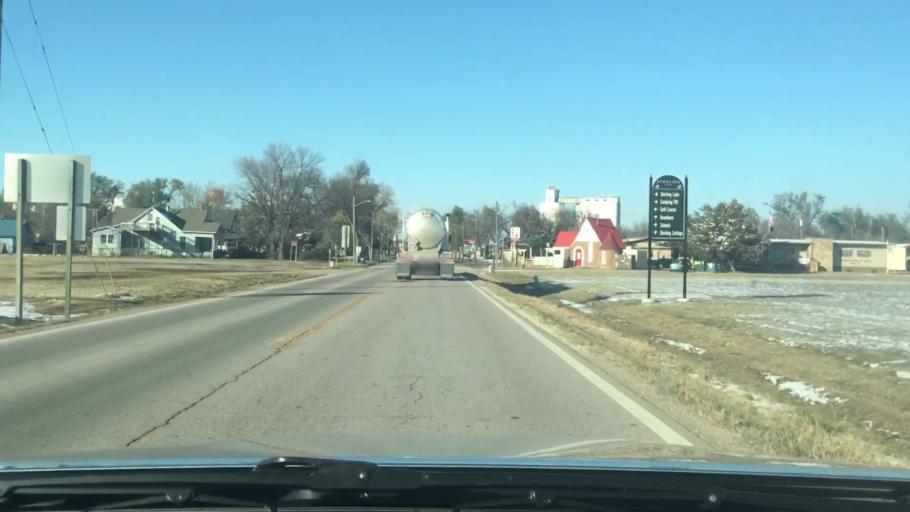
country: US
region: Kansas
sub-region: Rice County
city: Sterling
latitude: 38.2019
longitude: -98.2067
